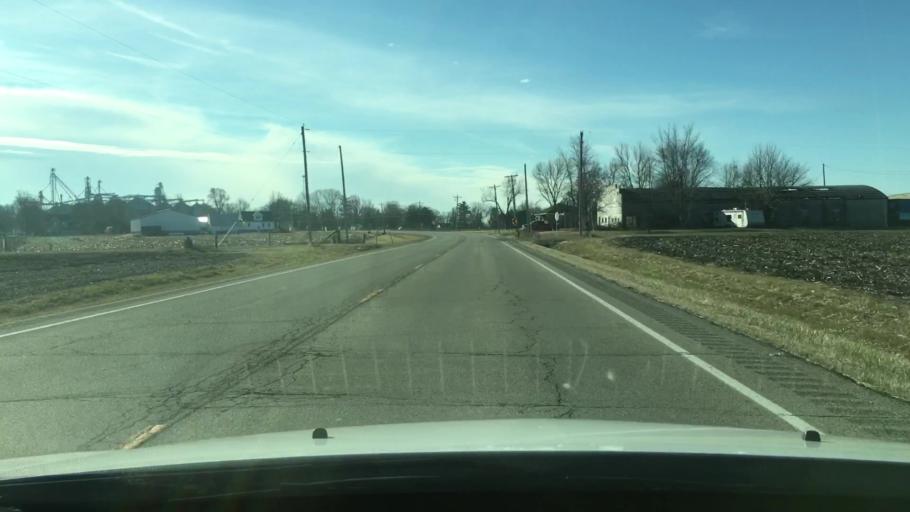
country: US
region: Illinois
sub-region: Marshall County
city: Toluca
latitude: 41.0435
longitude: -89.2276
